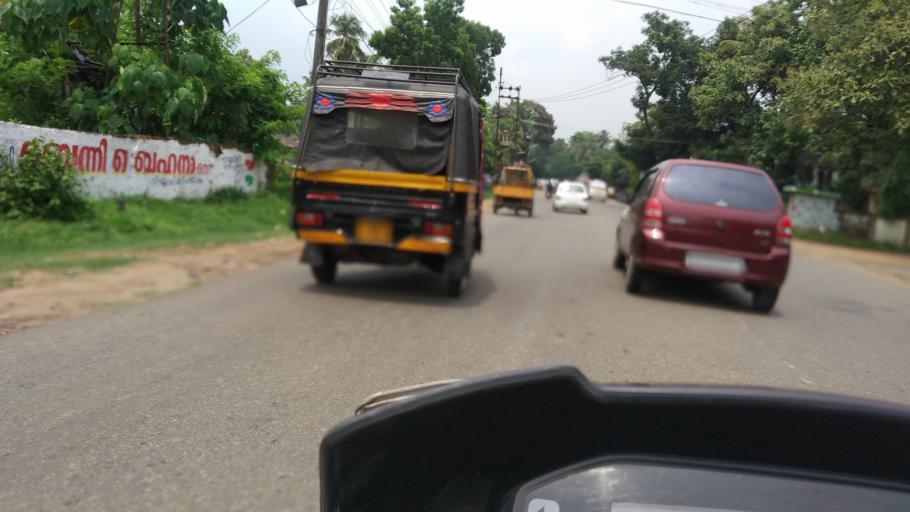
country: IN
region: Kerala
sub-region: Ernakulam
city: Perumpavur
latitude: 10.1135
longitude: 76.5065
